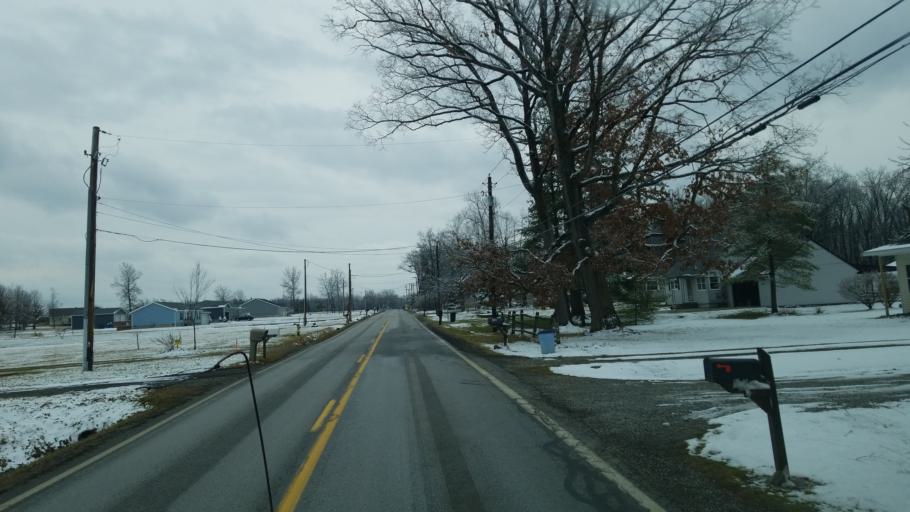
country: US
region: Ohio
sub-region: Portage County
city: Ravenna
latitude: 41.1623
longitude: -81.2135
